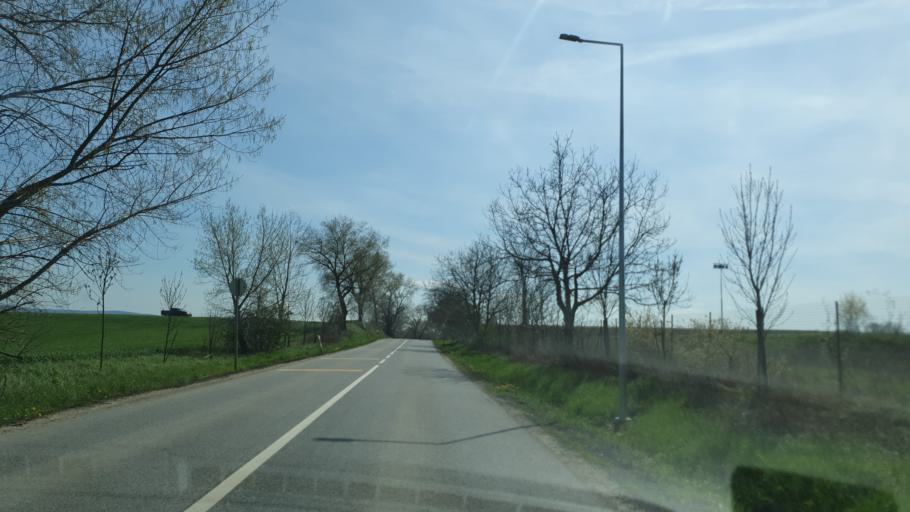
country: HU
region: Komarom-Esztergom
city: Bokod
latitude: 47.4890
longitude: 18.2421
